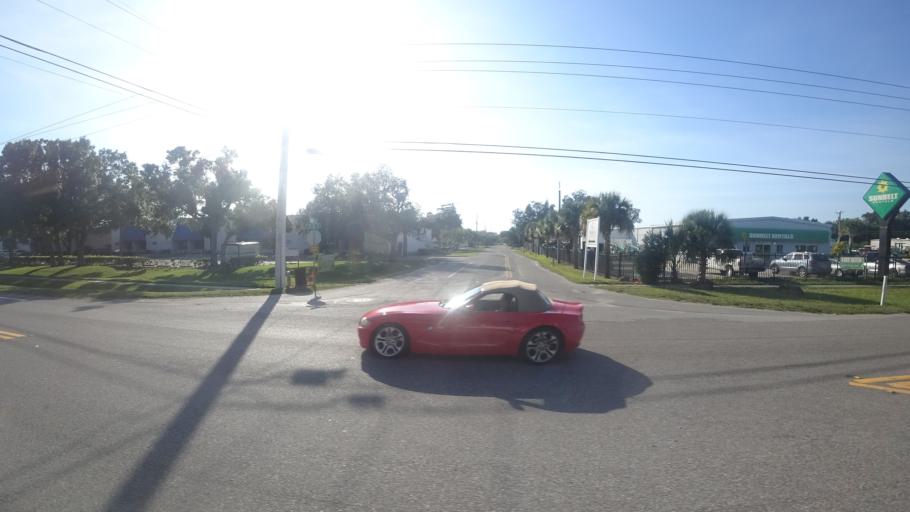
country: US
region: Florida
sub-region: Manatee County
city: Whitfield
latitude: 27.4053
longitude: -82.5468
